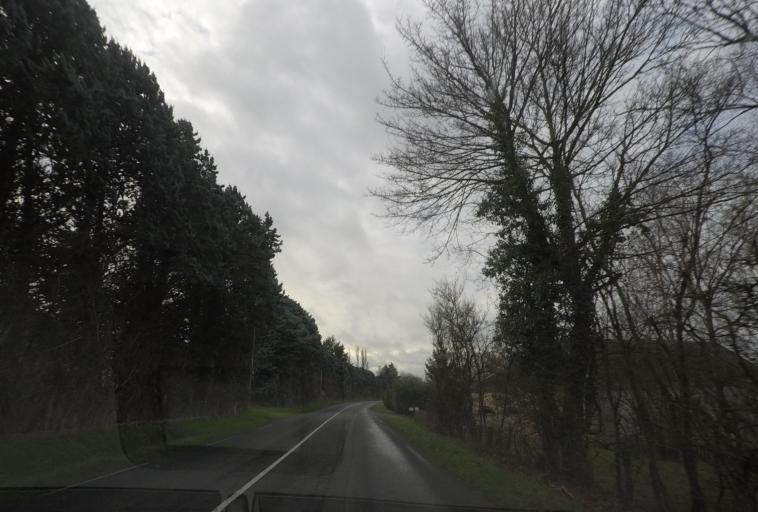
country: FR
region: Pays de la Loire
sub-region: Departement de la Sarthe
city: Saint-Calais
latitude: 47.9403
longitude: 0.7497
